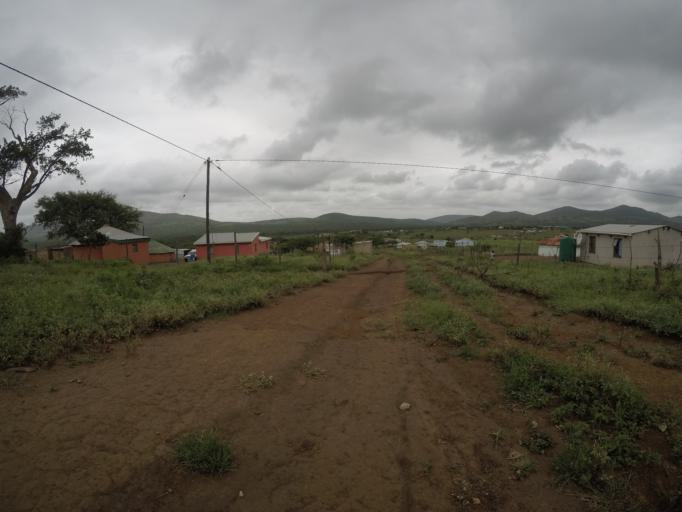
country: ZA
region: KwaZulu-Natal
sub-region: uThungulu District Municipality
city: Empangeni
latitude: -28.6011
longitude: 31.8653
